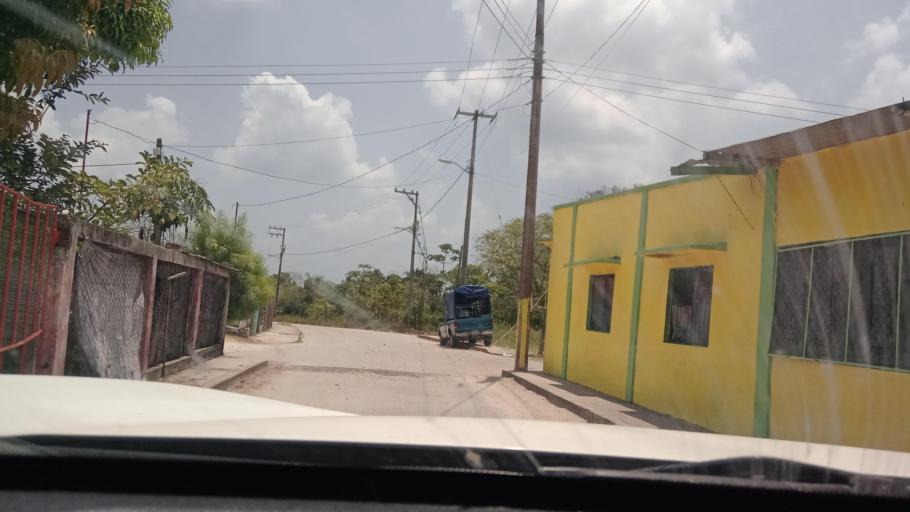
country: MX
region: Veracruz
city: Las Choapas
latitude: 17.9330
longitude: -94.1082
